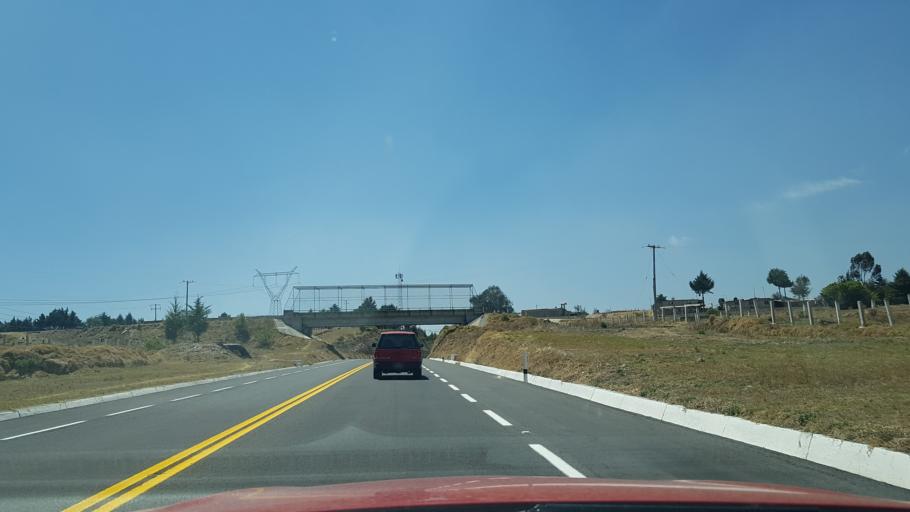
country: MX
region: Mexico
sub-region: Villa Victoria
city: Colonia Doctor Gustavo Baz
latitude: 19.3742
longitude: -99.9112
